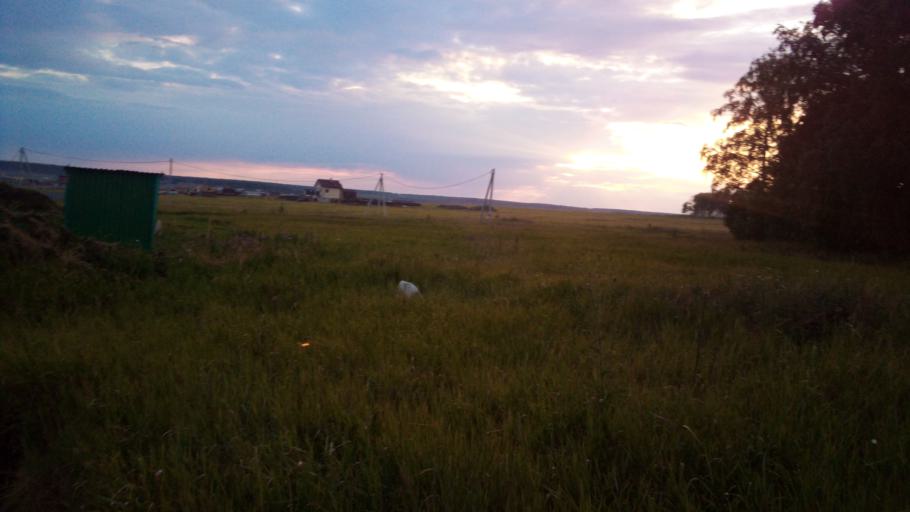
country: RU
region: Chelyabinsk
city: Roshchino
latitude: 55.2594
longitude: 61.0914
